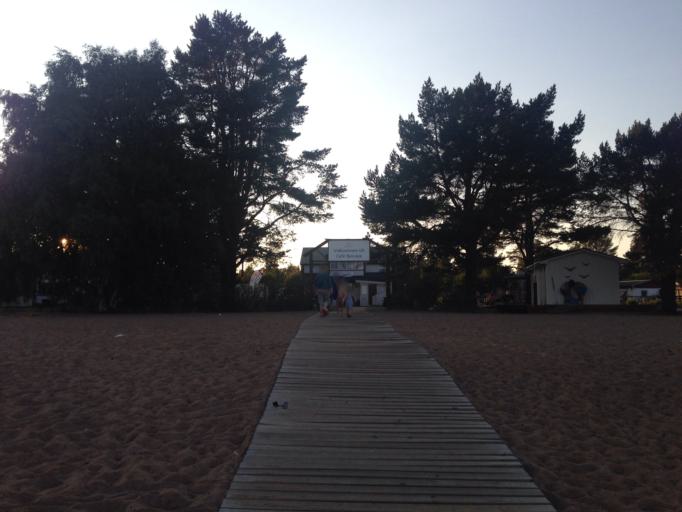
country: SE
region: Vaesterbotten
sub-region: Skelleftea Kommun
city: Byske
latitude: 64.9464
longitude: 21.2380
